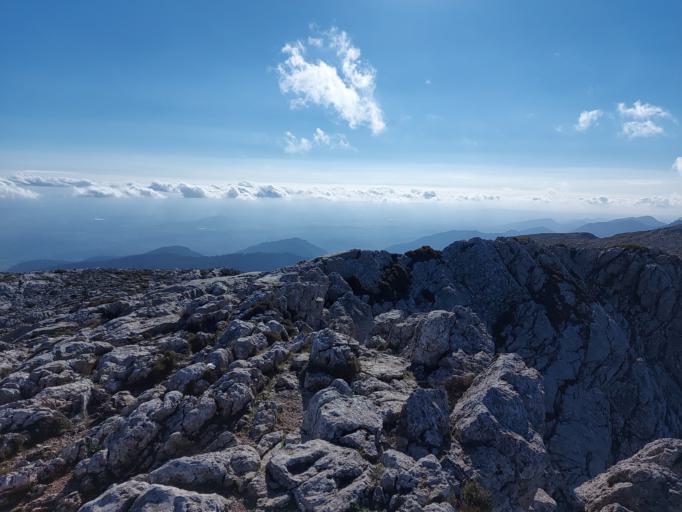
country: ES
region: Balearic Islands
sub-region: Illes Balears
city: Escorca
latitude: 39.8432
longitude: 2.9257
